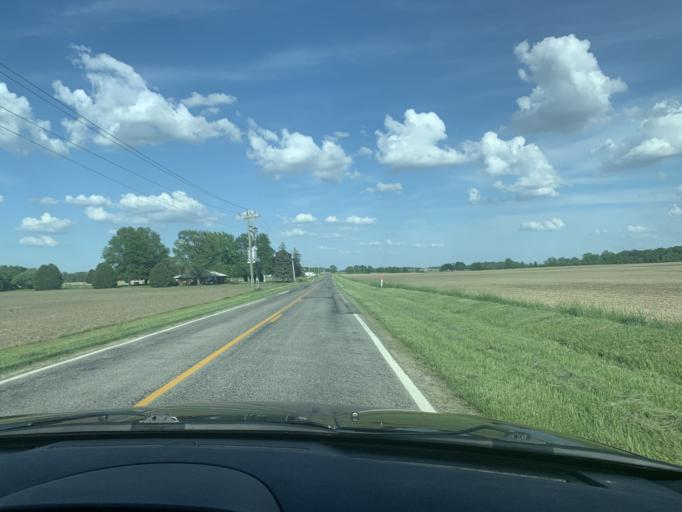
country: US
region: Ohio
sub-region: Logan County
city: De Graff
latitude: 40.2407
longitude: -83.9560
